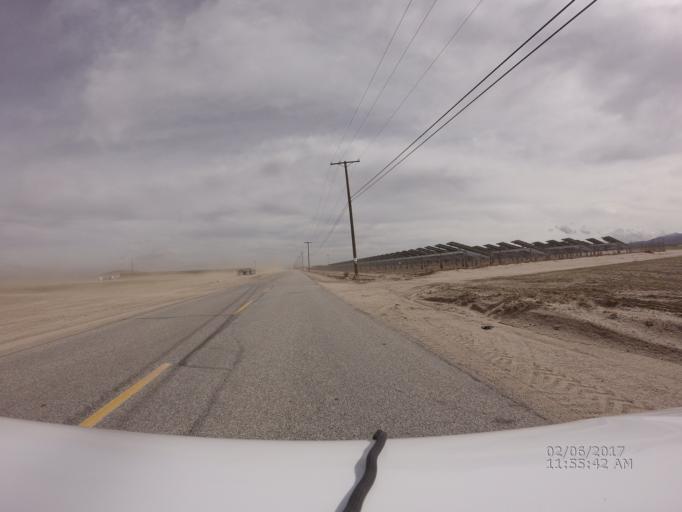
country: US
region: California
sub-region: San Bernardino County
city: Pinon Hills
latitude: 34.5651
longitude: -117.6956
